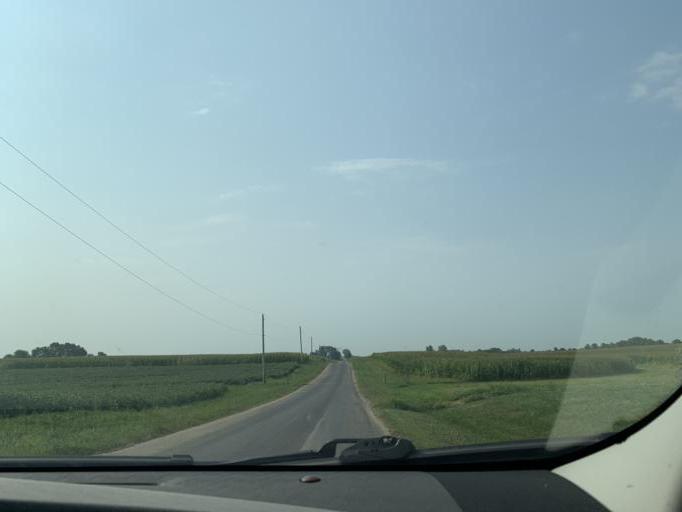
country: US
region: Illinois
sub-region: Whiteside County
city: Sterling
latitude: 41.8416
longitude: -89.7470
